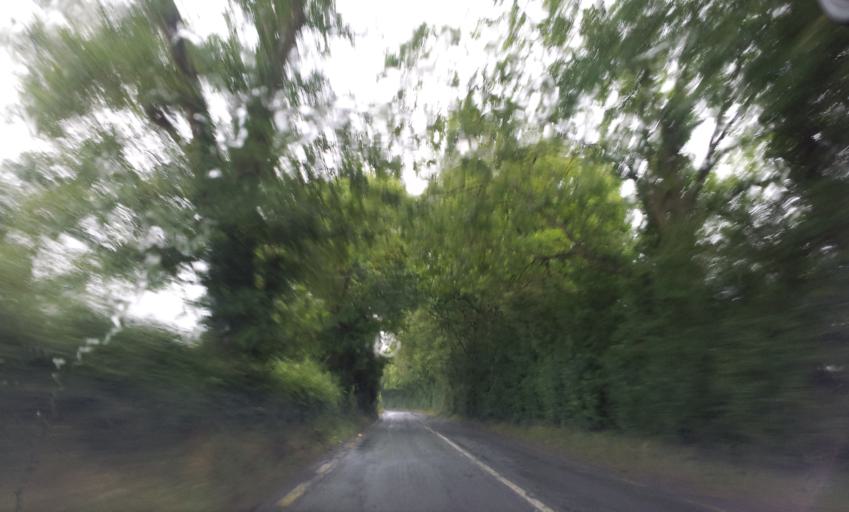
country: IE
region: Munster
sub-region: County Cork
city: Mallow
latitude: 52.1497
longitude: -8.6208
